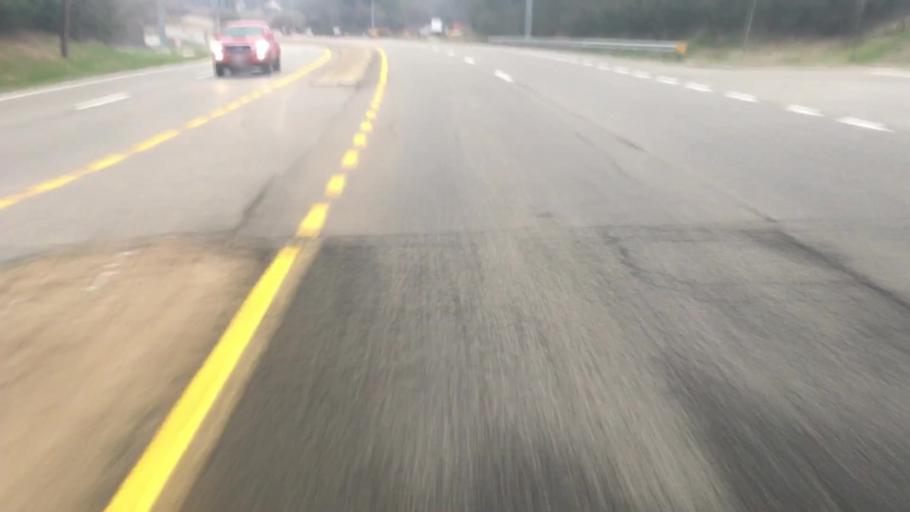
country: US
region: Alabama
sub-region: Jefferson County
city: Fultondale
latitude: 33.5773
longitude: -86.8056
